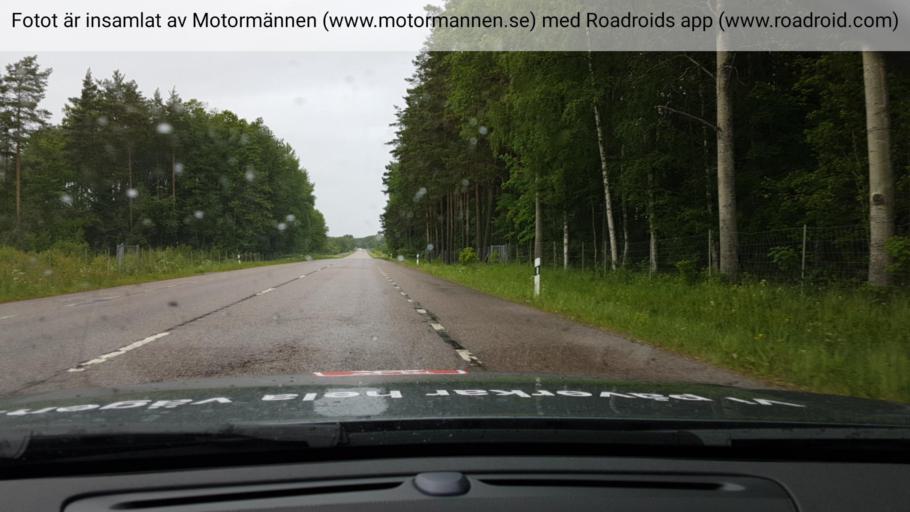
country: SE
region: Uppsala
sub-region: Alvkarleby Kommun
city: AElvkarleby
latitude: 60.5738
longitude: 17.4665
